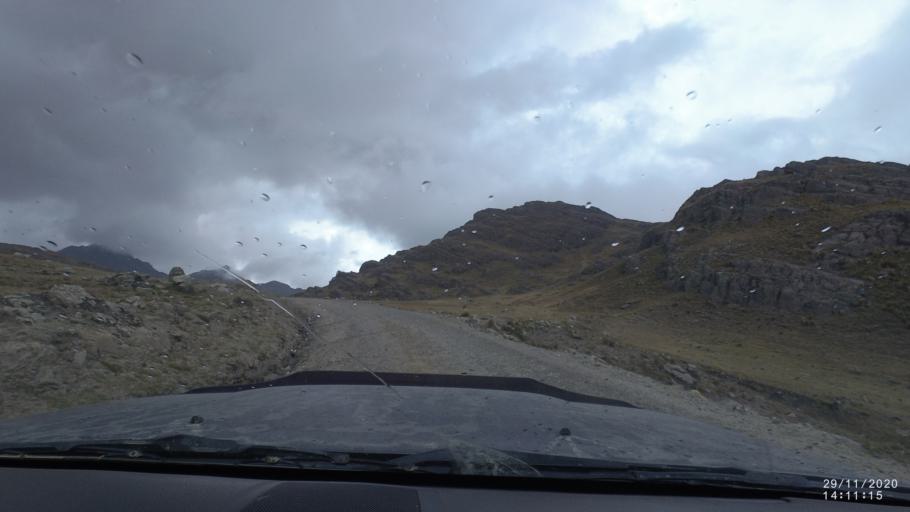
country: BO
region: Cochabamba
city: Sipe Sipe
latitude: -17.2332
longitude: -66.3924
